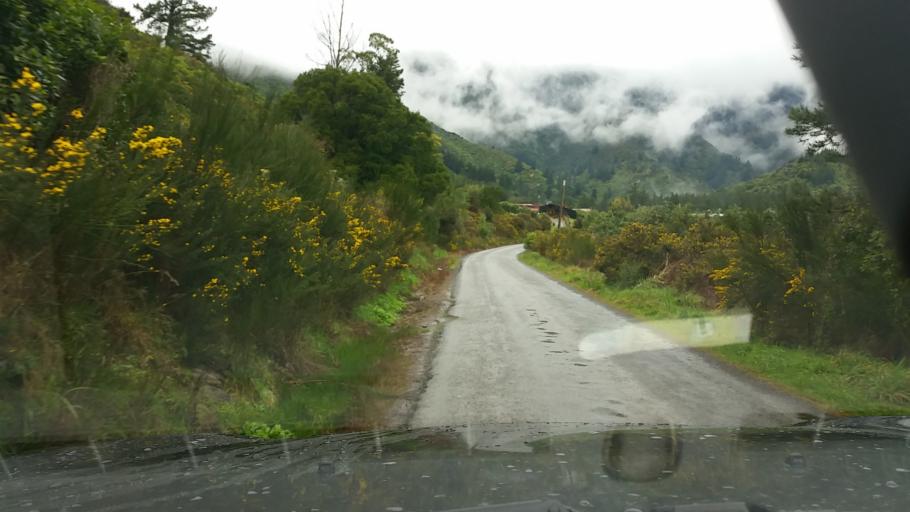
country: NZ
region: Marlborough
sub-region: Marlborough District
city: Picton
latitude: -41.2824
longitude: 174.0329
